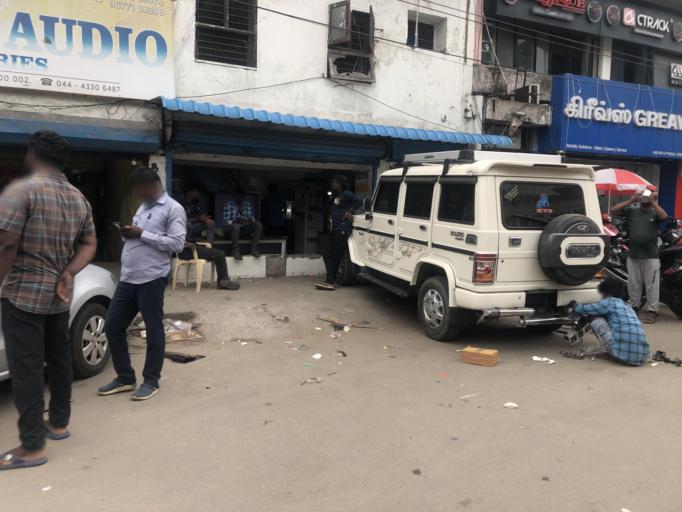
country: IN
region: Tamil Nadu
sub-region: Chennai
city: Chetput
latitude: 13.0613
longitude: 80.2653
